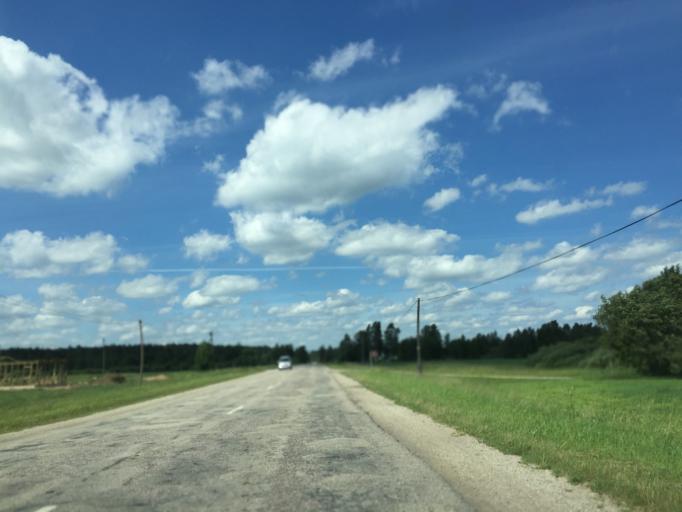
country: LV
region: Engure
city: Smarde
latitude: 56.9607
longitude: 23.3341
